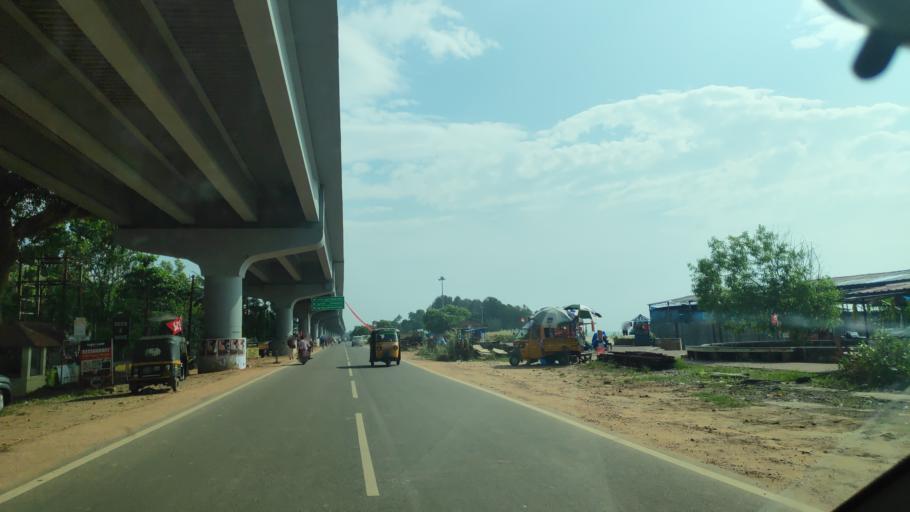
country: IN
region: Kerala
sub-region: Alappuzha
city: Alleppey
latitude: 9.4911
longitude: 76.3191
